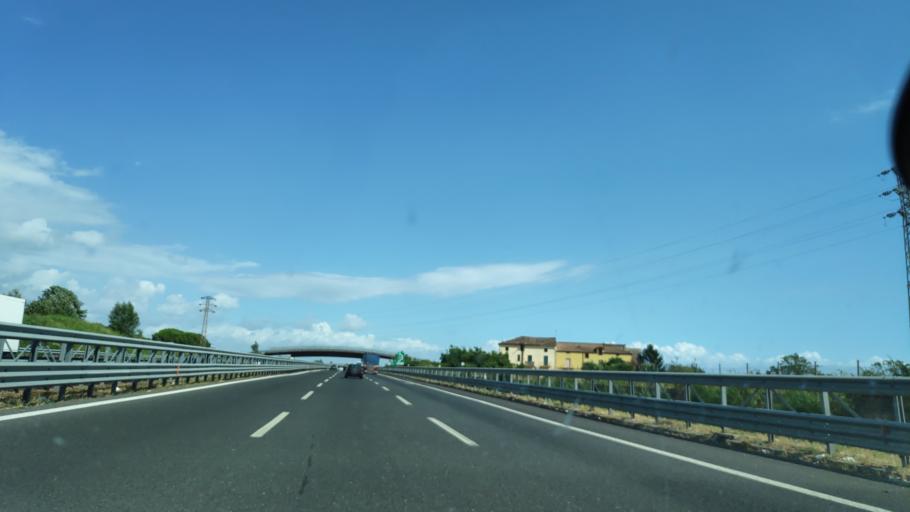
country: IT
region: Campania
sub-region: Provincia di Salerno
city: Pontecagnano
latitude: 40.6497
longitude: 14.8800
